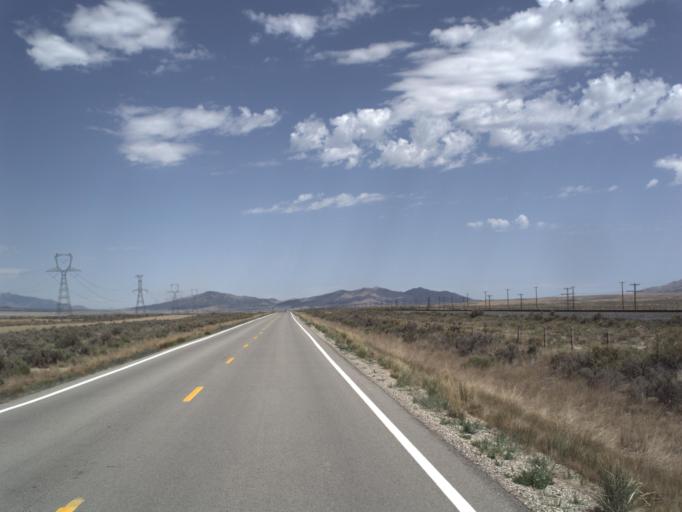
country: US
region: Utah
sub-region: Tooele County
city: Tooele
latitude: 40.2812
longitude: -112.3988
